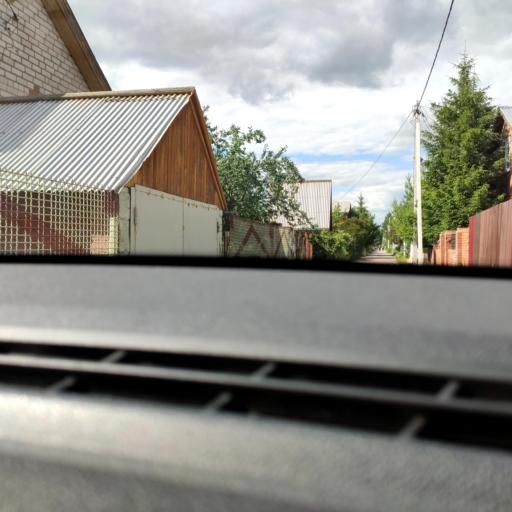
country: RU
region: Samara
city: Podstepki
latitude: 53.5806
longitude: 49.0735
